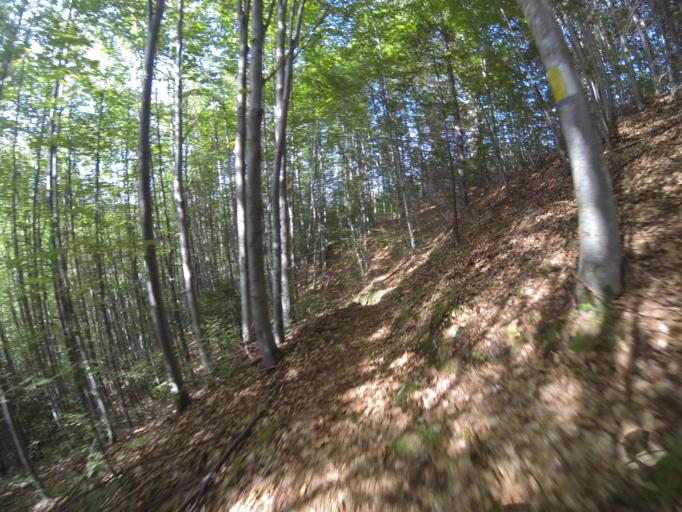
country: RO
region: Valcea
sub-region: Comuna Barbatesti
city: Barbatesti
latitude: 45.2628
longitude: 24.1518
